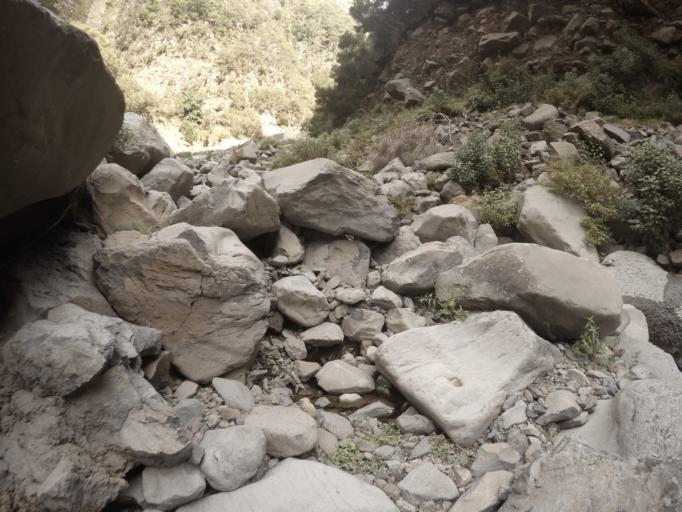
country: PT
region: Madeira
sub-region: Funchal
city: Nossa Senhora do Monte
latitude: 32.7020
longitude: -16.9201
